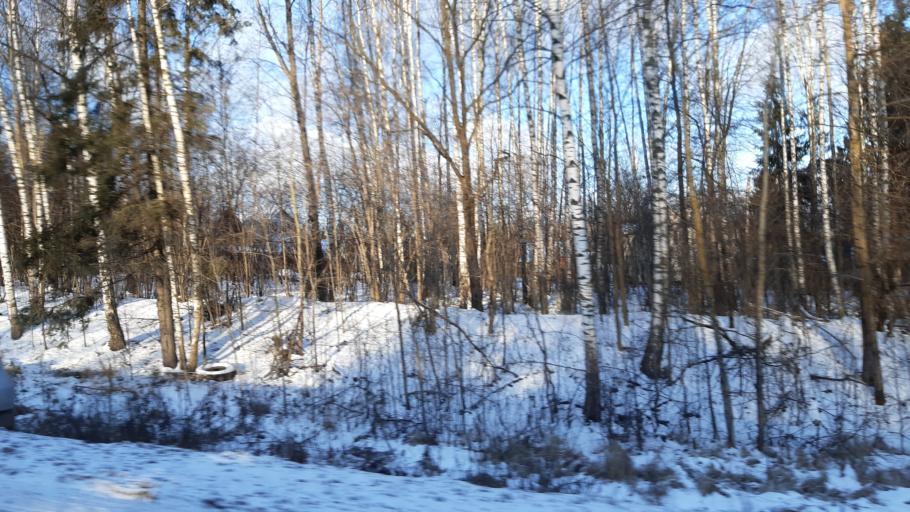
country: RU
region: Vladimir
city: Arsaki
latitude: 56.2978
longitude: 38.3591
